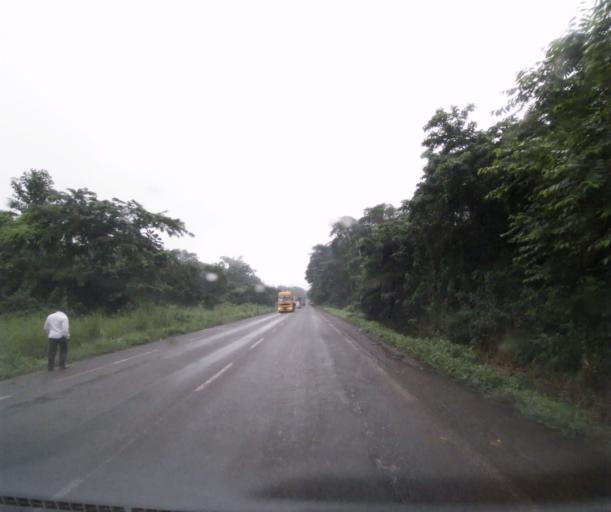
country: CM
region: Centre
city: Eseka
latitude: 3.8915
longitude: 10.7685
